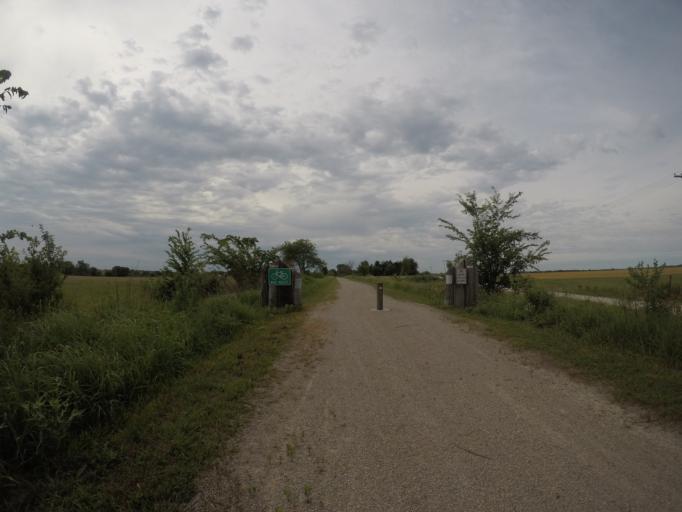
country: US
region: Kansas
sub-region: Franklin County
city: Ottawa
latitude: 38.4508
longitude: -95.2670
